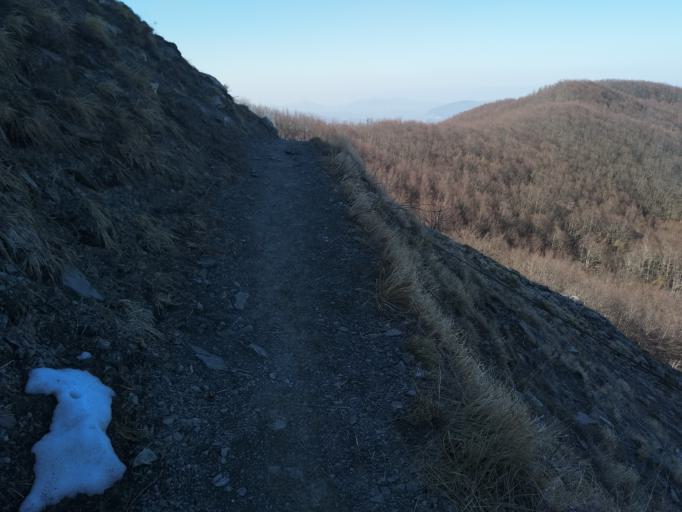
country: IT
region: Emilia-Romagna
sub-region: Provincia di Reggio Emilia
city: Busana
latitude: 44.3813
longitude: 10.2954
